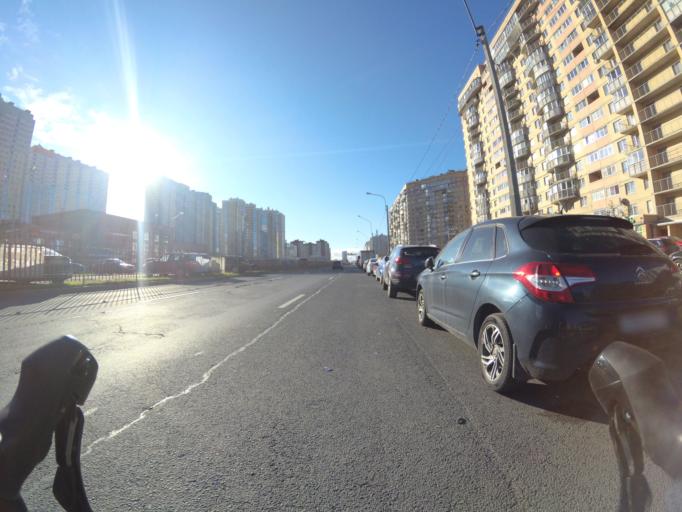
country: RU
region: Leningrad
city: Untolovo
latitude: 60.0053
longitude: 30.2113
